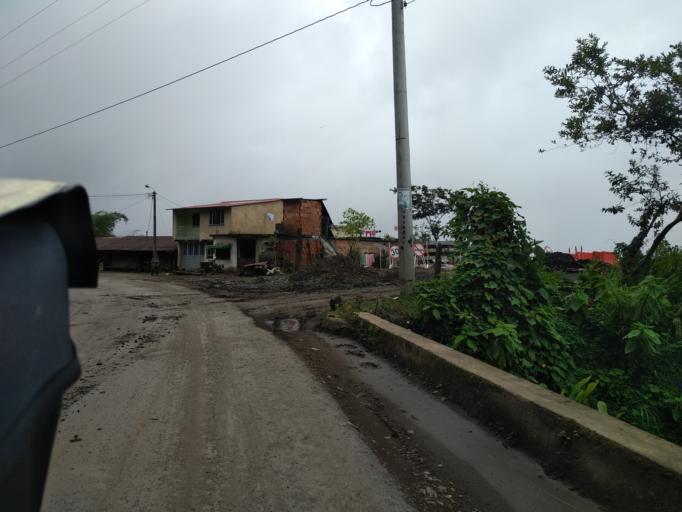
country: CO
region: Santander
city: Landazuri
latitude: 6.1791
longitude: -73.7151
